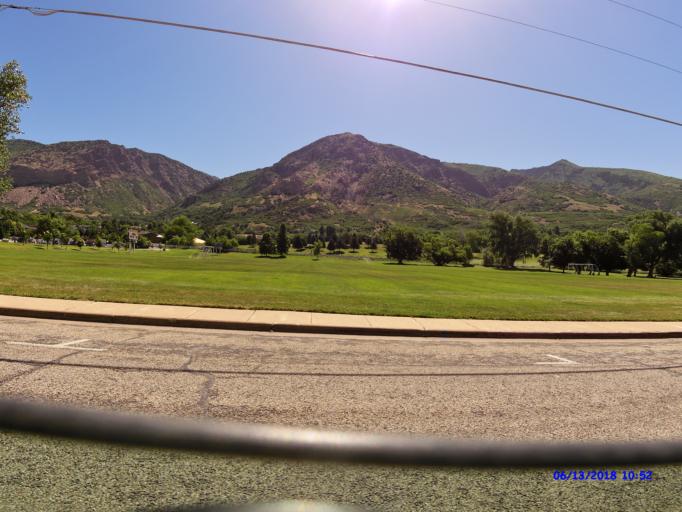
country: US
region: Utah
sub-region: Weber County
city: South Ogden
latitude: 41.2092
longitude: -111.9403
